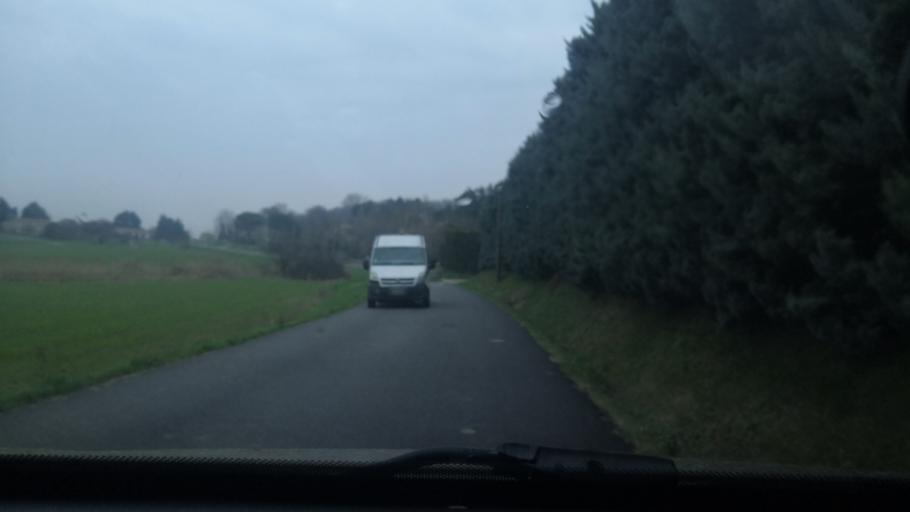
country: FR
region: Rhone-Alpes
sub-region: Departement de la Drome
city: Montboucher-sur-Jabron
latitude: 44.5538
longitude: 4.8131
